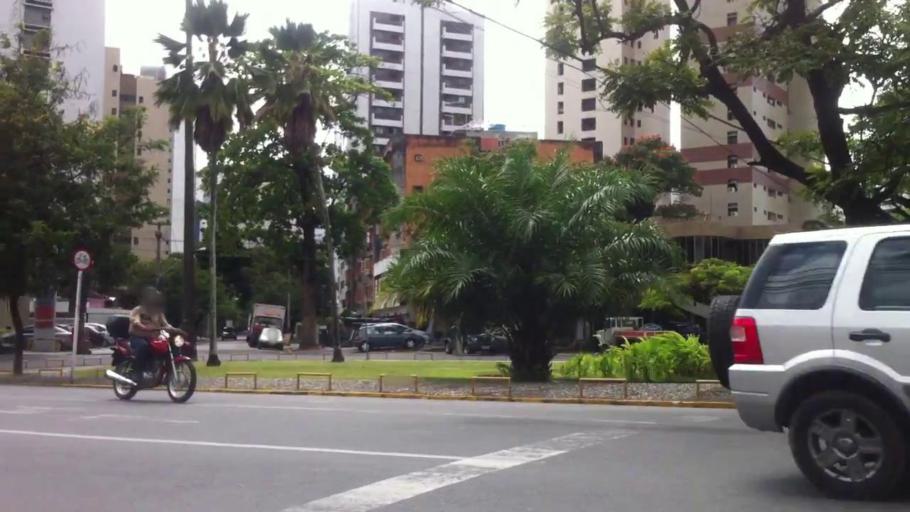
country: BR
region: Pernambuco
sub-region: Recife
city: Recife
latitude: -8.0334
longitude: -34.9100
